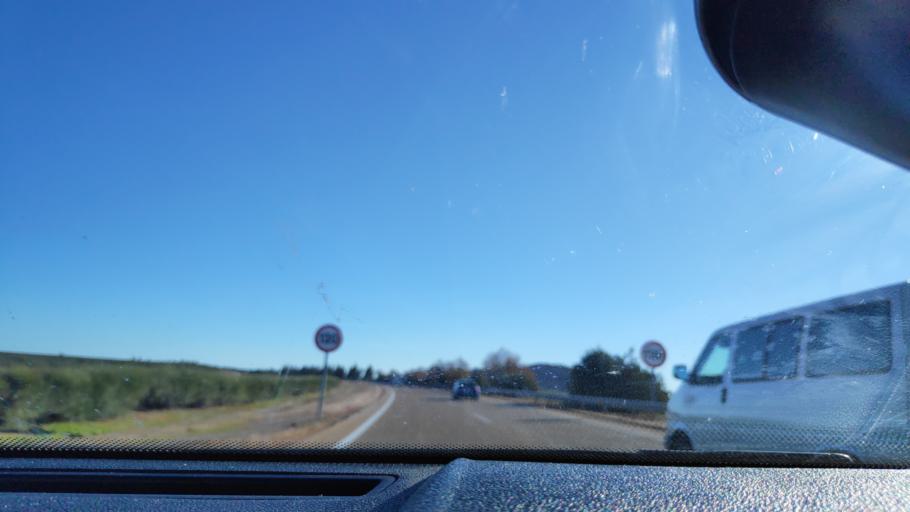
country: ES
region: Extremadura
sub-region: Provincia de Badajoz
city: Los Santos de Maimona
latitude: 38.4695
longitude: -6.3605
